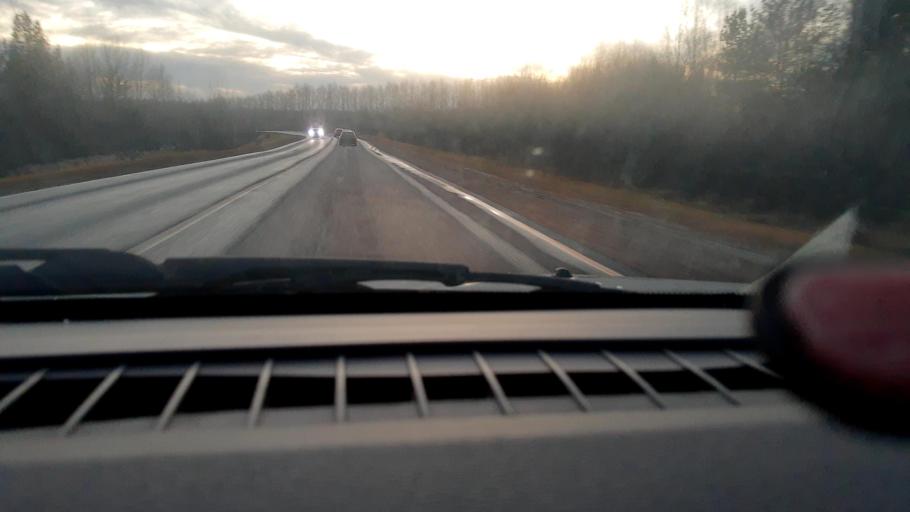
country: RU
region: Nizjnij Novgorod
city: Vladimirskoye
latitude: 56.9585
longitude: 45.0998
